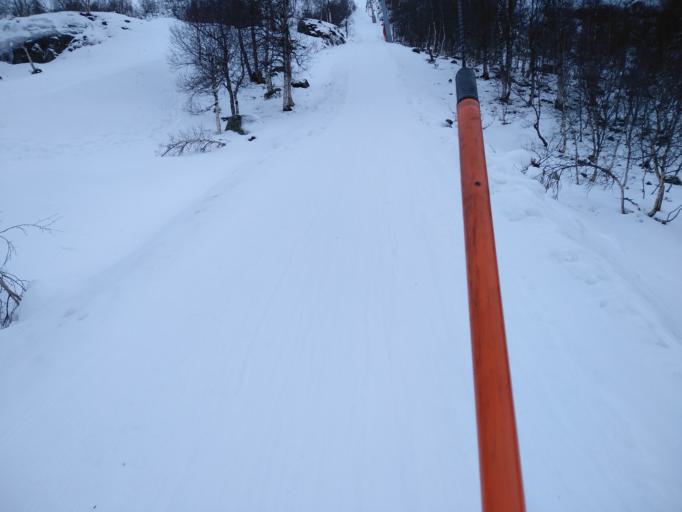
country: NO
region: Vest-Agder
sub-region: Sirdal
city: Tonstad
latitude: 59.0227
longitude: 6.9193
